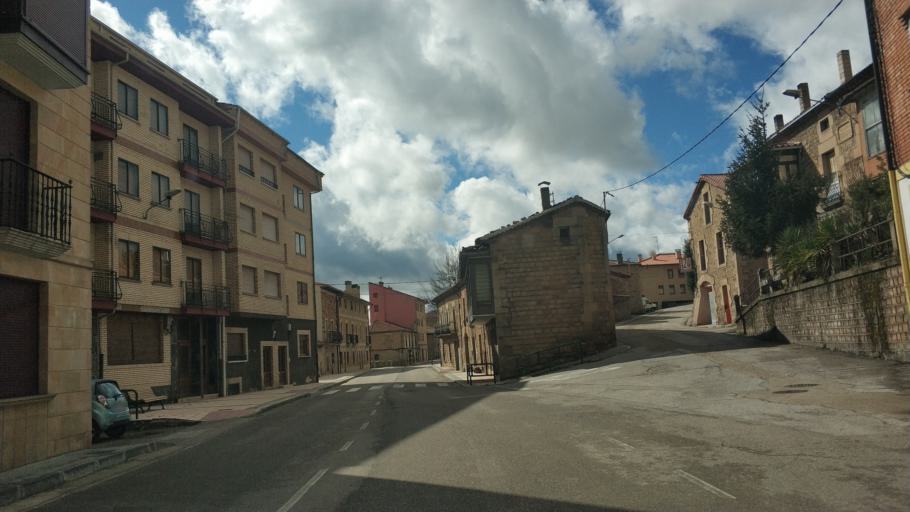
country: ES
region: Castille and Leon
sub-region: Provincia de Burgos
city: Quintanar de la Sierra
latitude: 41.9828
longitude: -3.0368
